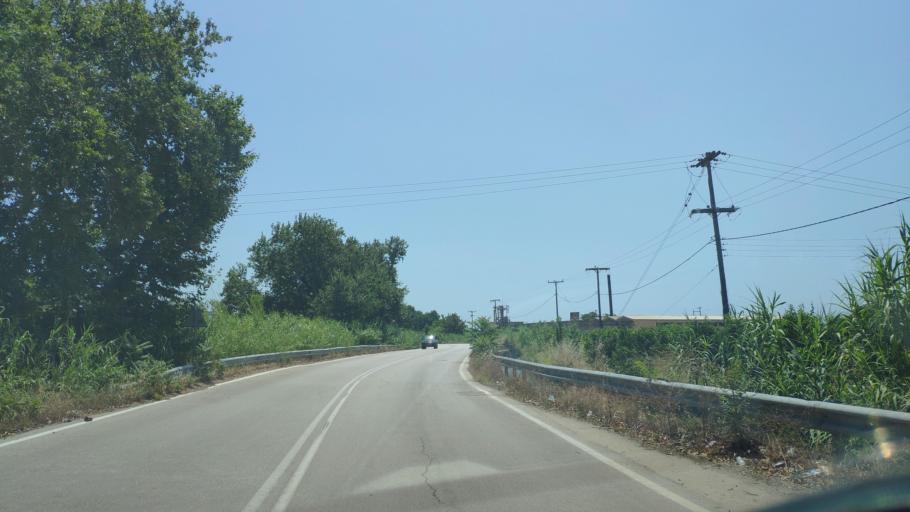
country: GR
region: Epirus
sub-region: Nomos Artas
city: Arta
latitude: 39.1503
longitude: 20.9750
